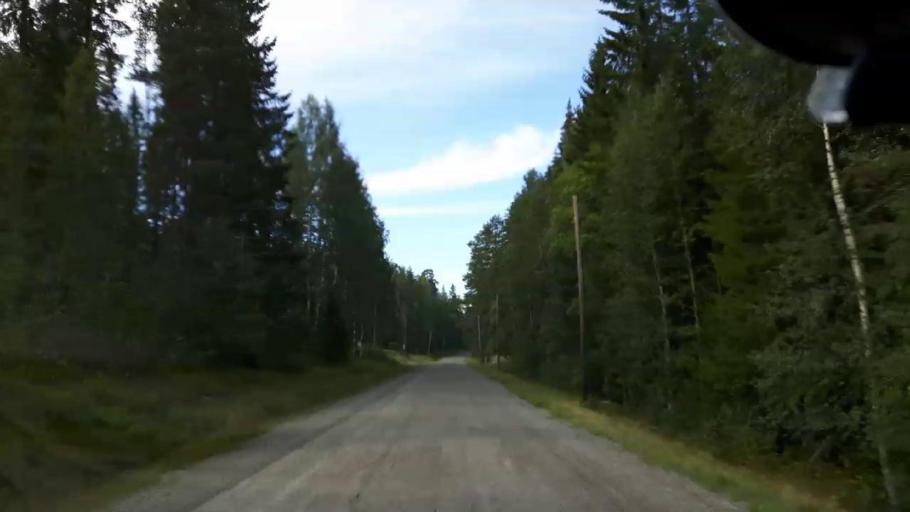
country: SE
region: Jaemtland
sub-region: Ragunda Kommun
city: Hammarstrand
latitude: 63.1256
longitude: 15.9765
